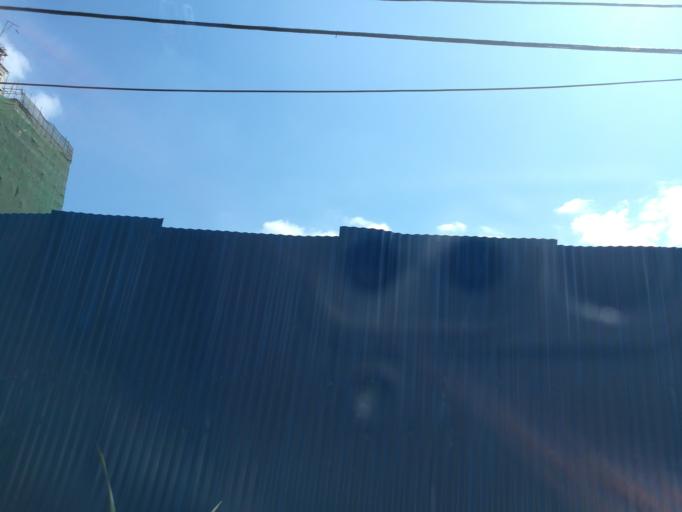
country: KE
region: Nairobi Area
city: Nairobi
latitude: -1.2978
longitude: 36.7907
